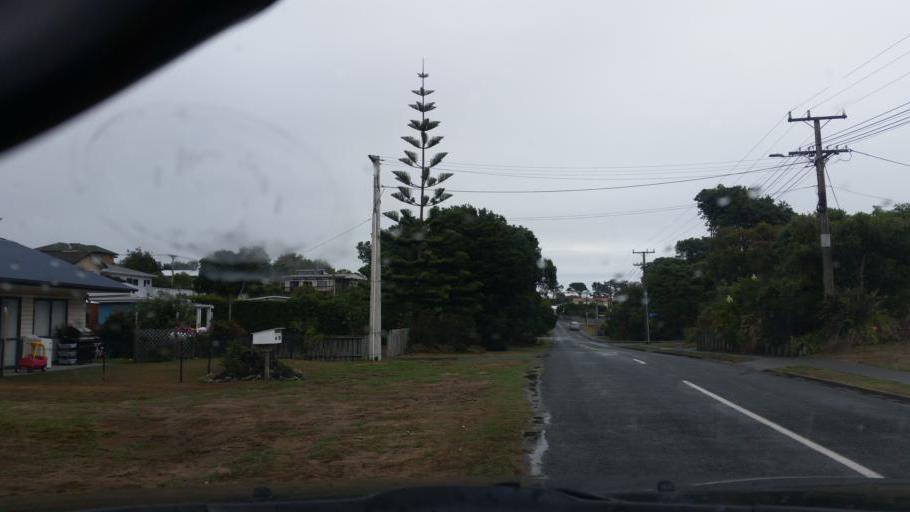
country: NZ
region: Auckland
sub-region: Auckland
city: Wellsford
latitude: -36.0936
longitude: 174.5903
